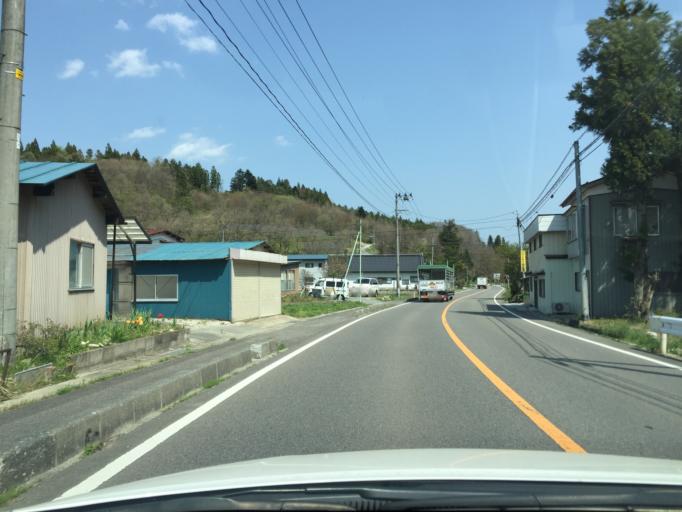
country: JP
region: Fukushima
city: Funehikimachi-funehiki
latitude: 37.4586
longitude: 140.7258
